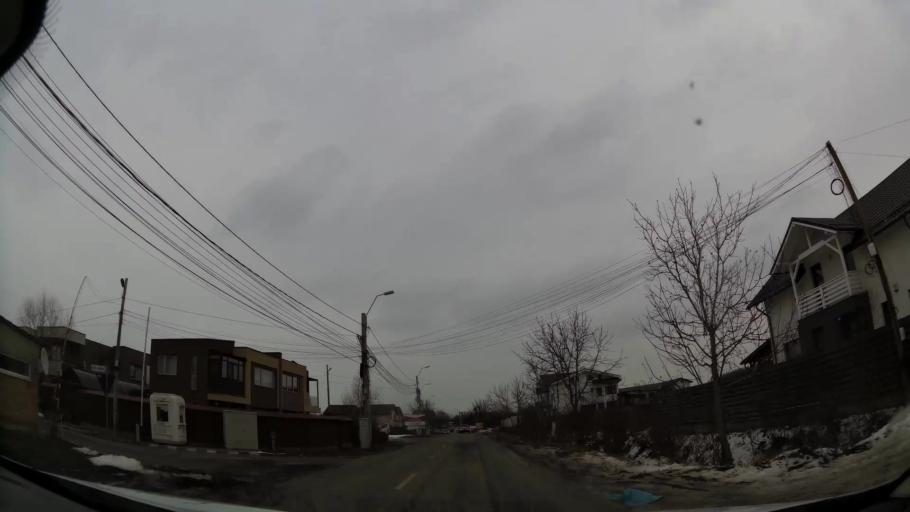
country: RO
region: Ilfov
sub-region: Comuna Tunari
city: Tunari
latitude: 44.5495
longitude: 26.1226
